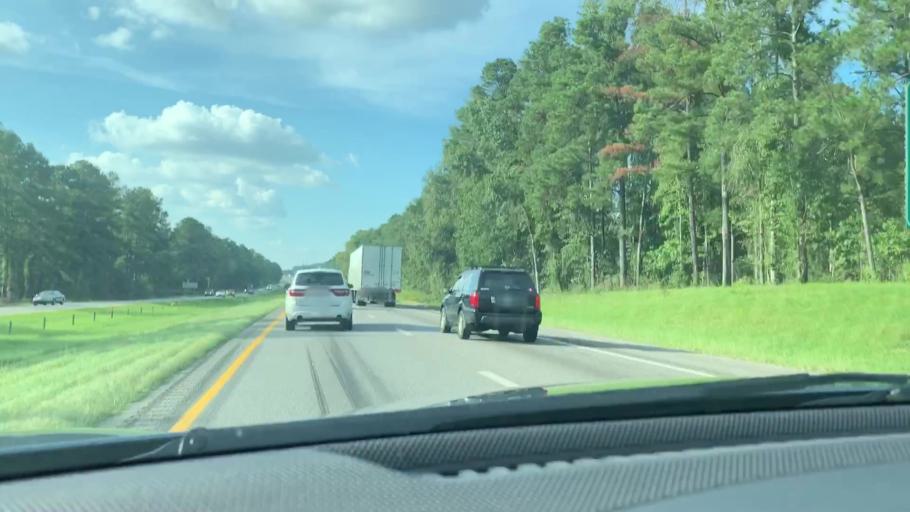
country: US
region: South Carolina
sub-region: Orangeburg County
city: Brookdale
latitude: 33.5454
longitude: -80.8127
